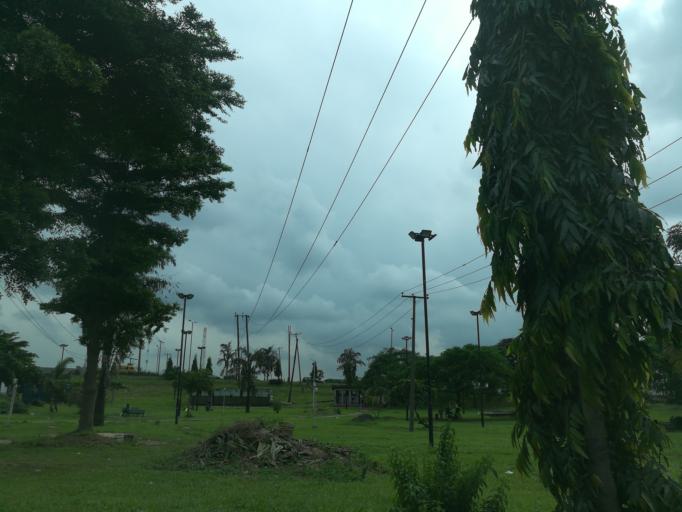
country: NG
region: Lagos
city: Ojota
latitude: 6.5920
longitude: 3.3827
